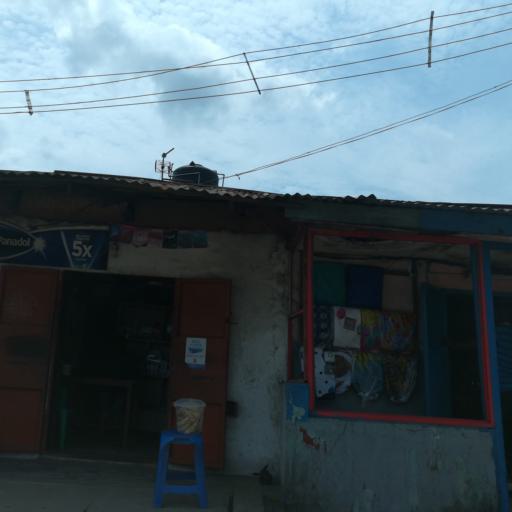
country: NG
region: Rivers
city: Port Harcourt
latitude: 4.7781
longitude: 7.0412
